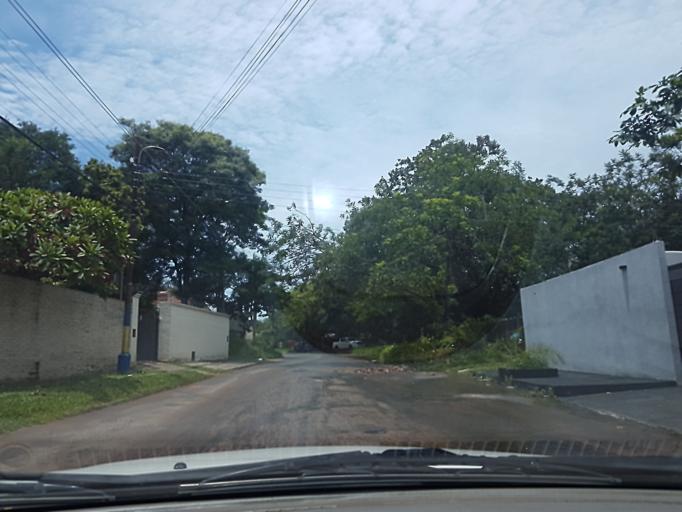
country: PY
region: Central
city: San Lorenzo
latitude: -25.2547
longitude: -57.5062
